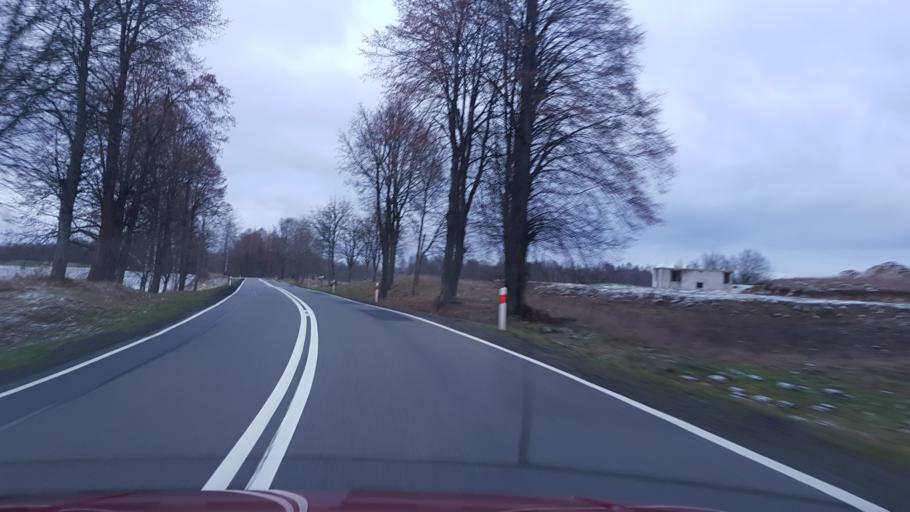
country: PL
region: Pomeranian Voivodeship
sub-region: Powiat bytowski
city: Tuchomie
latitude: 54.0813
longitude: 17.2982
